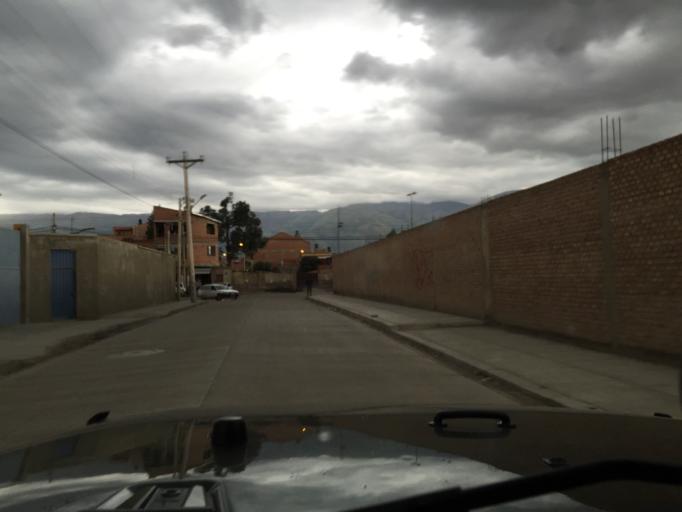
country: BO
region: Cochabamba
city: Cochabamba
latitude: -17.3978
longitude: -66.2124
